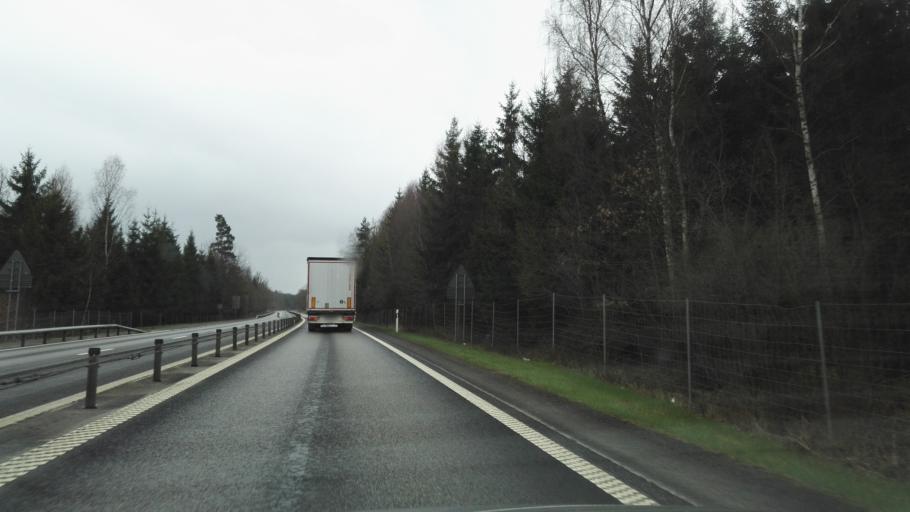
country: SE
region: Skane
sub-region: Osby Kommun
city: Osby
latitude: 56.3361
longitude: 14.0108
